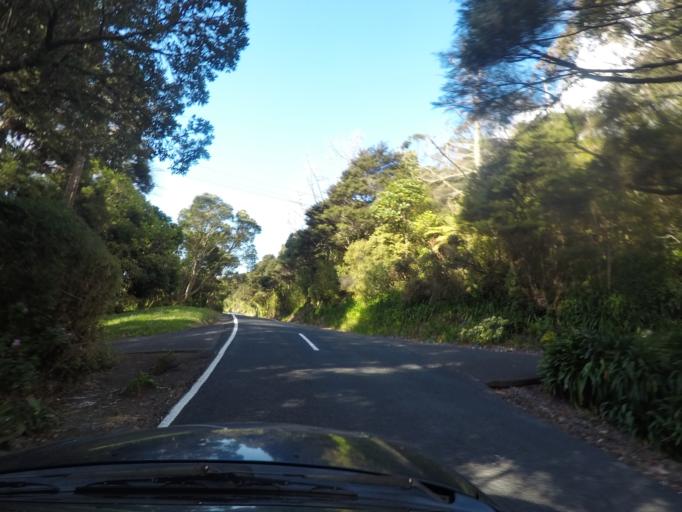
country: NZ
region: Auckland
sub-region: Auckland
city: Titirangi
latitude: -36.9402
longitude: 174.6219
